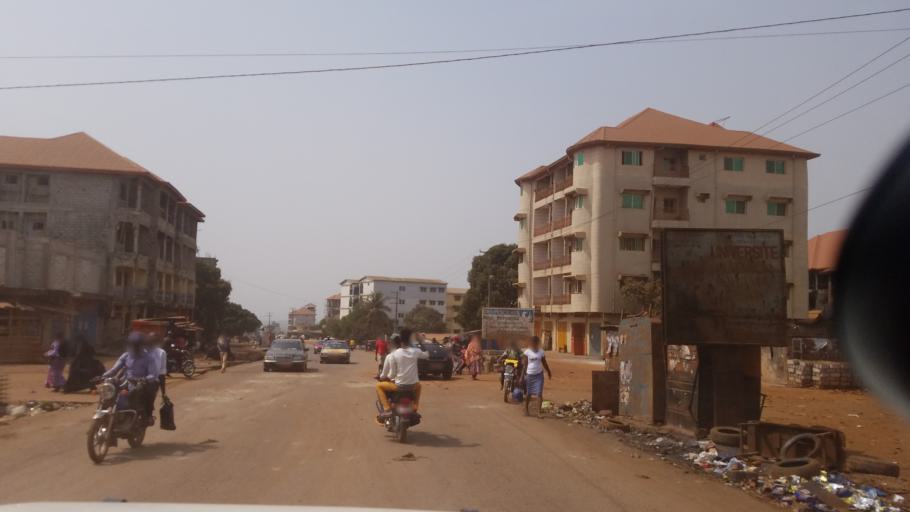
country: GN
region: Kindia
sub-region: Prefecture de Dubreka
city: Dubreka
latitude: 9.6699
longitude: -13.5589
